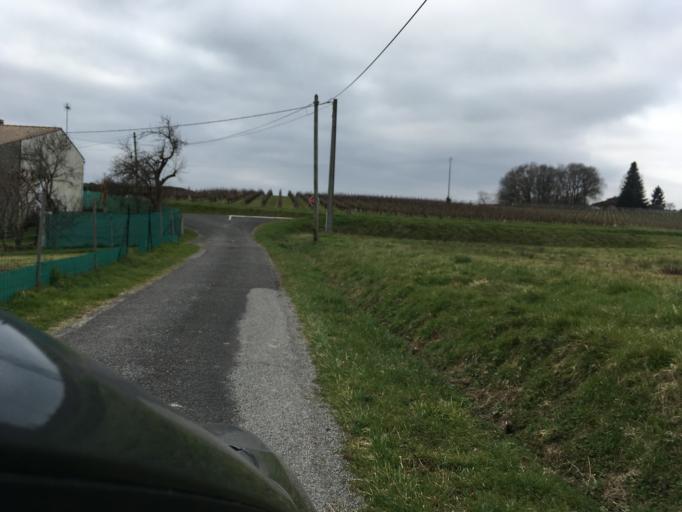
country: FR
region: Poitou-Charentes
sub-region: Departement de la Charente-Maritime
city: Mirambeau
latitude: 45.3309
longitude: -0.5875
